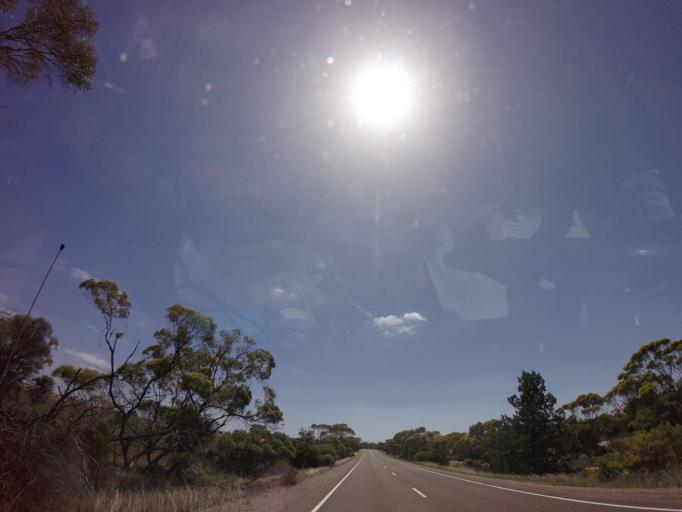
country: AU
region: South Australia
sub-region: Kimba
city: Caralue
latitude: -33.2154
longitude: 136.3481
